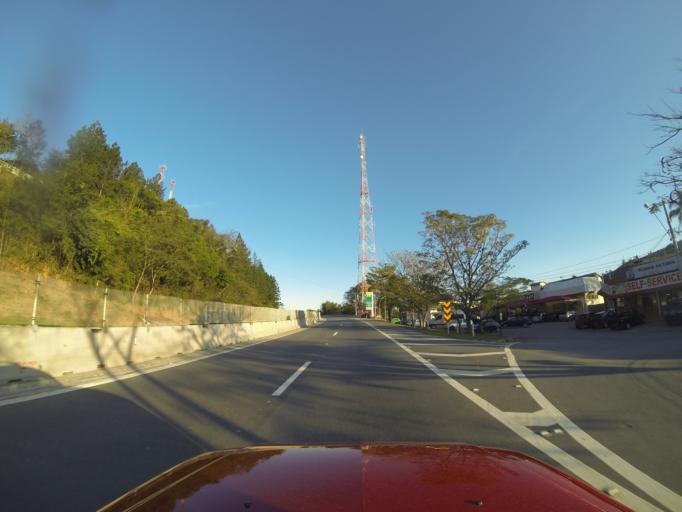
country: BR
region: Sao Paulo
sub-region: Santa Branca
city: Santa Branca
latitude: -23.3825
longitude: -45.6621
